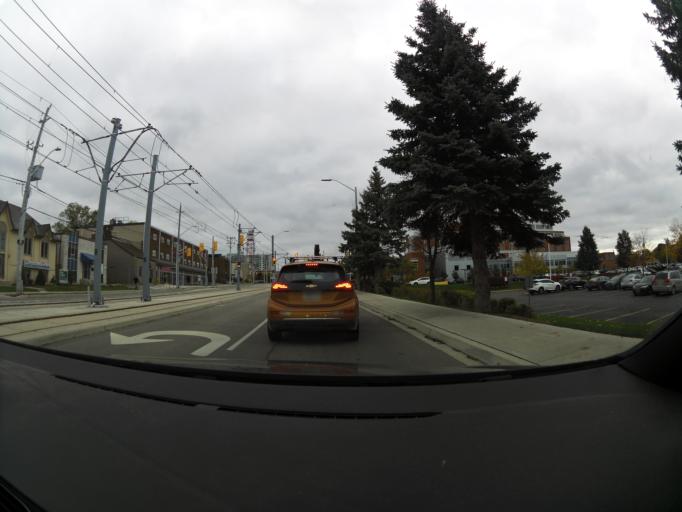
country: CA
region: Ontario
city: Waterloo
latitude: 43.4578
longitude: -80.5140
